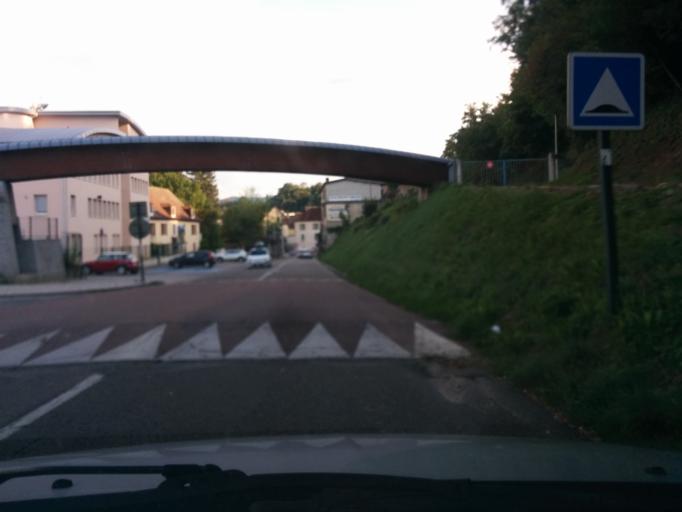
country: FR
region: Rhone-Alpes
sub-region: Departement de la Savoie
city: Le Pont-de-Beauvoisin
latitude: 45.5393
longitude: 5.6685
